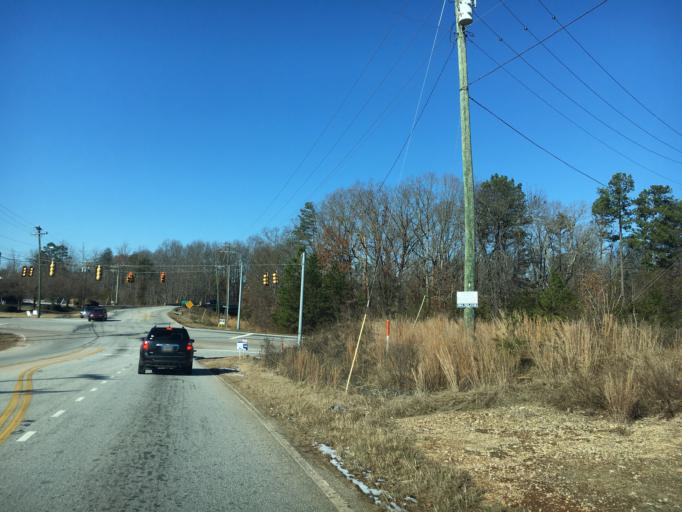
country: US
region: South Carolina
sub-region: Greenville County
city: Taylors
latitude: 34.9163
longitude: -82.2657
